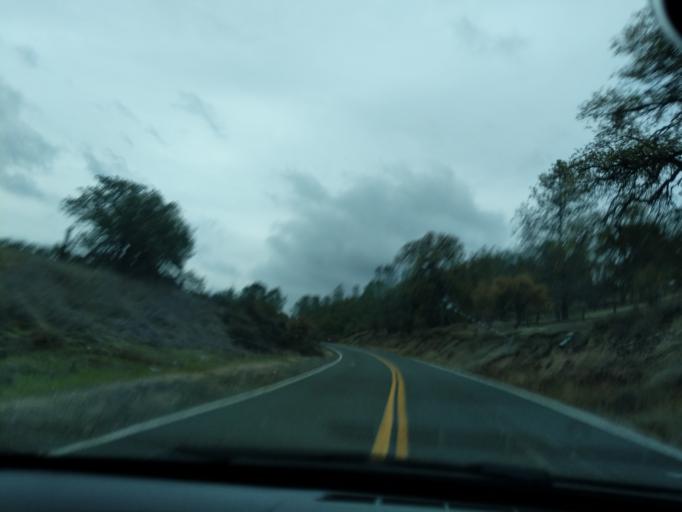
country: US
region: California
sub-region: Monterey County
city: Soledad
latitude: 36.5852
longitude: -121.1951
